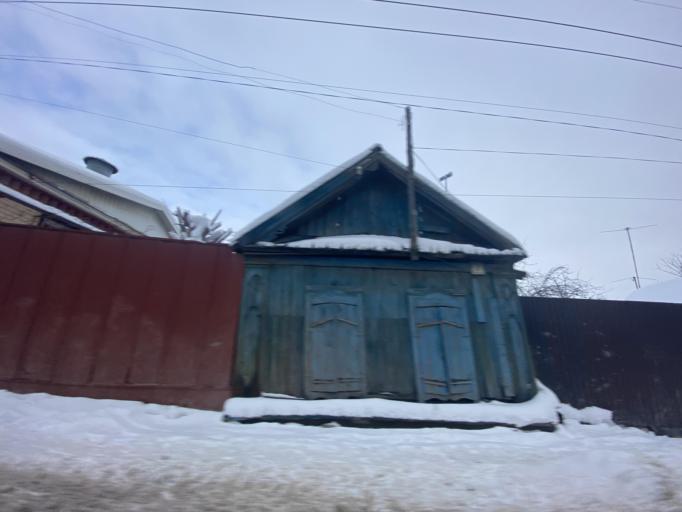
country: RU
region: Saratov
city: Engel's
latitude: 51.5020
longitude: 46.1065
